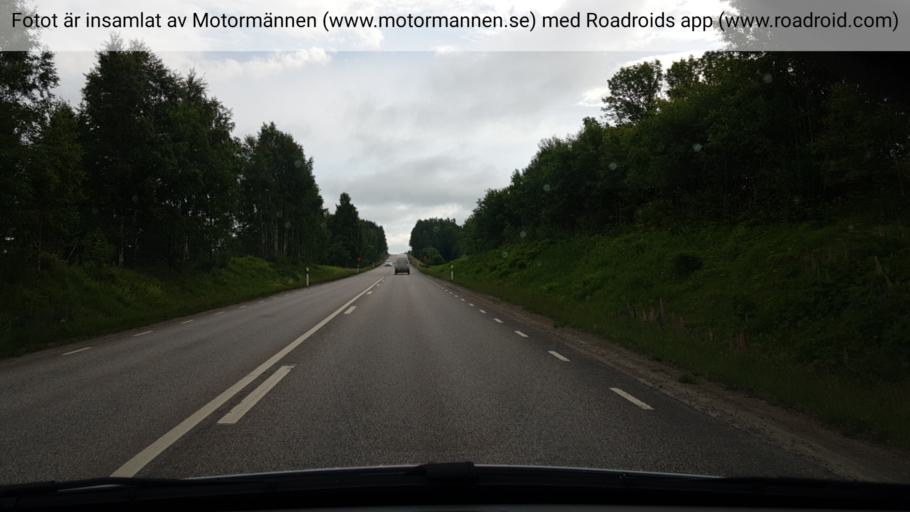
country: SE
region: Vaestra Goetaland
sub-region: Karlsborgs Kommun
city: Molltorp
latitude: 58.4658
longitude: 14.2970
